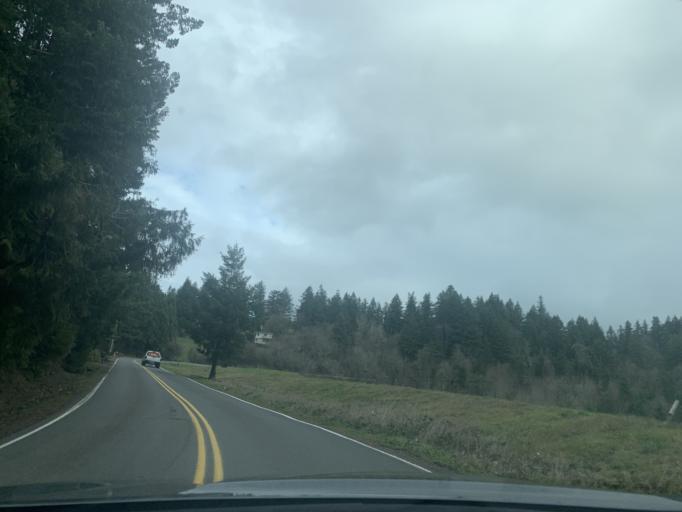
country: US
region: Oregon
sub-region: Washington County
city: Cedar Mill
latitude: 45.5663
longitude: -122.8067
